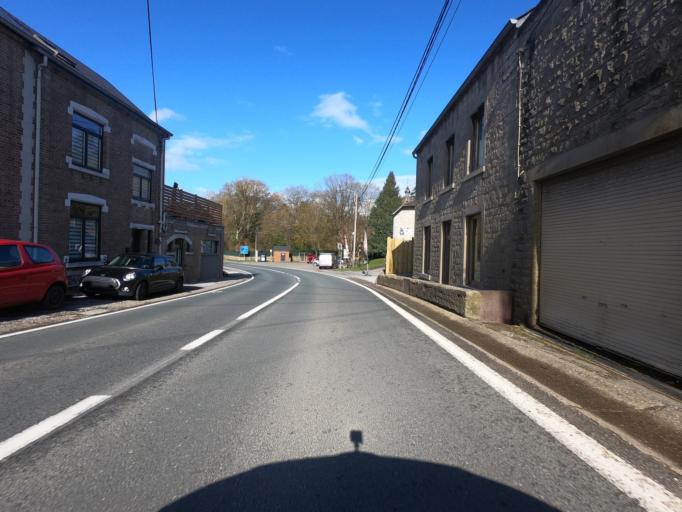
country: BE
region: Wallonia
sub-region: Province de Namur
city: Mettet
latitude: 50.2989
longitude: 4.7212
